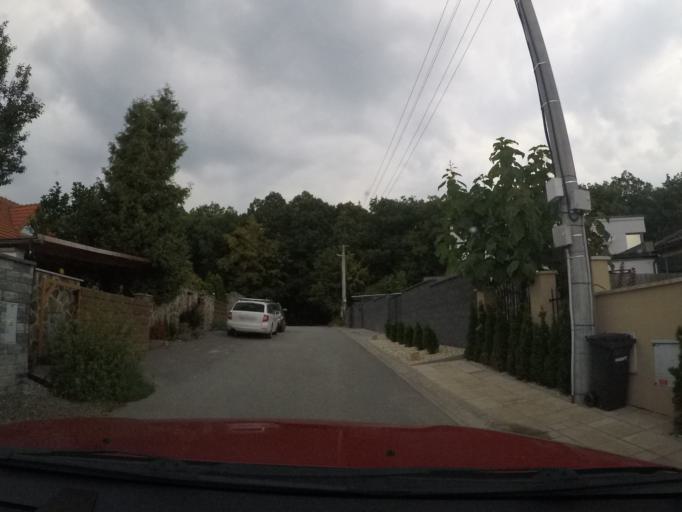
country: SK
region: Kosicky
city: Kosice
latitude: 48.6955
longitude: 21.2074
